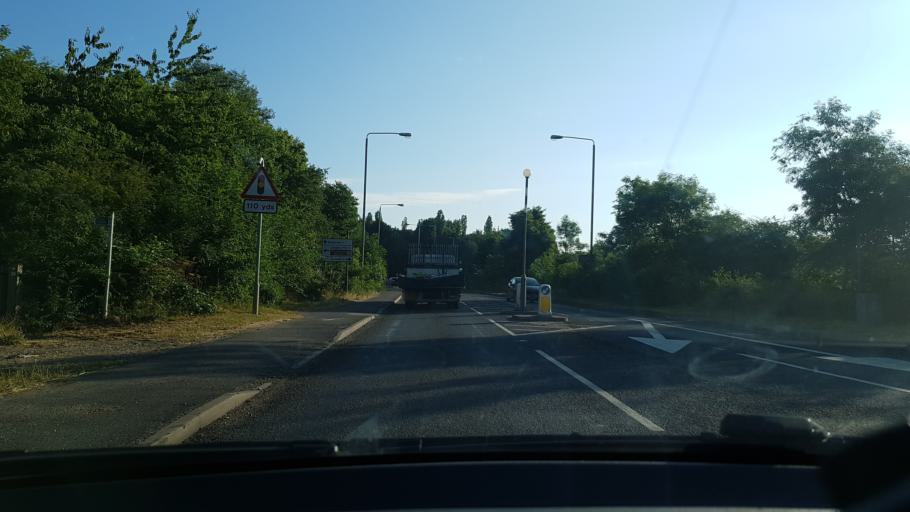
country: GB
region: England
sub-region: Nottinghamshire
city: Awsworth
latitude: 52.9981
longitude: -1.2806
